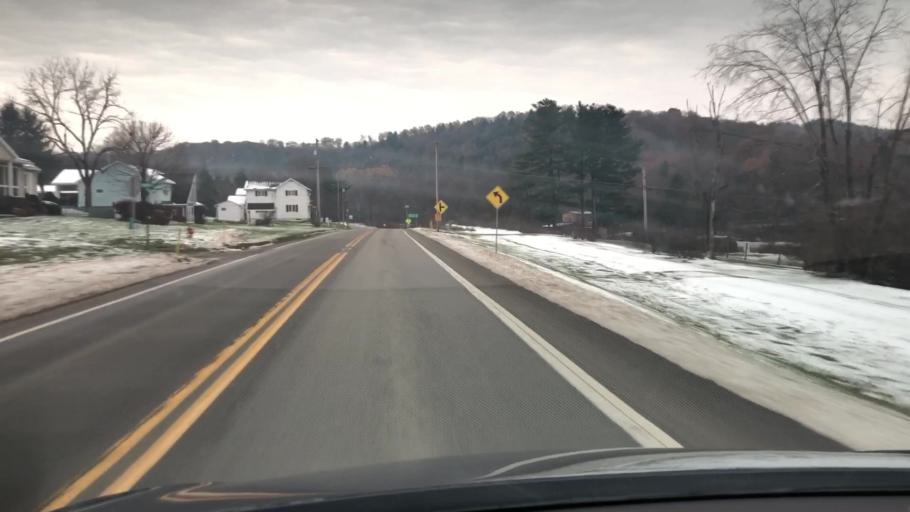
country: US
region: Pennsylvania
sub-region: Clarion County
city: Clarion
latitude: 41.0121
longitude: -79.2921
